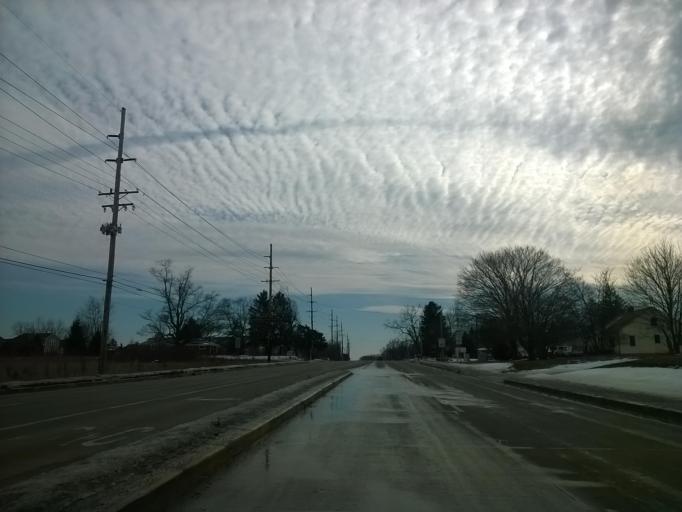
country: US
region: Indiana
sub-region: Boone County
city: Zionsville
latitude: 39.9623
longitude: -86.2472
